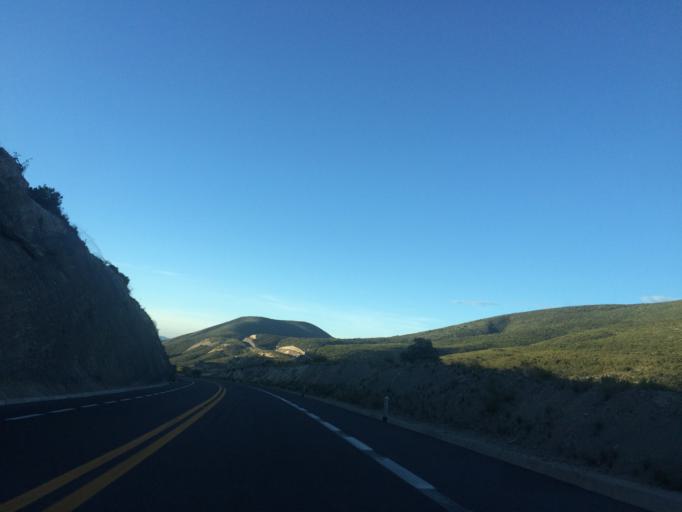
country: MX
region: Puebla
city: Chapuco
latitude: 18.6746
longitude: -97.4602
